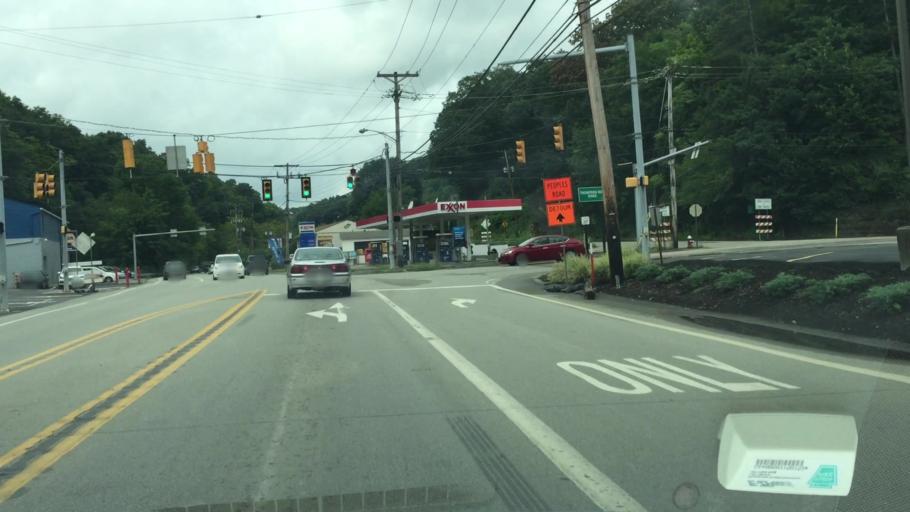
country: US
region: Pennsylvania
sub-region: Allegheny County
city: Glenshaw
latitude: 40.5108
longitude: -79.9936
